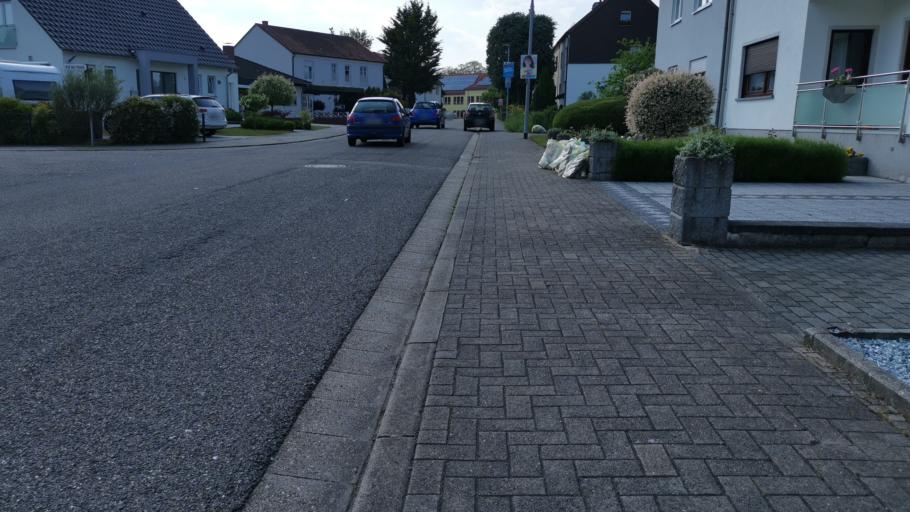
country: DE
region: Saarland
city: Spiesen-Elversberg
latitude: 49.2791
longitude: 7.1675
